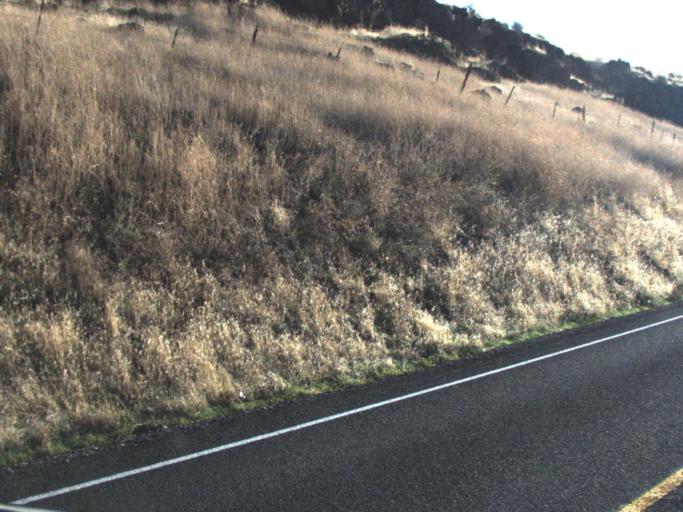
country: US
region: Washington
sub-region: Garfield County
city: Pomeroy
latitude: 46.4963
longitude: -117.7720
